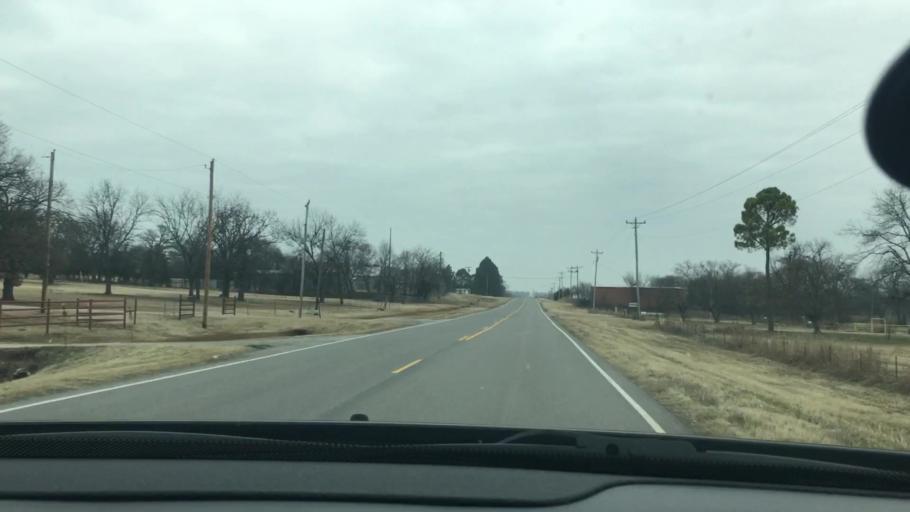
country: US
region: Oklahoma
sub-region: Carter County
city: Healdton
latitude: 34.2553
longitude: -97.4923
